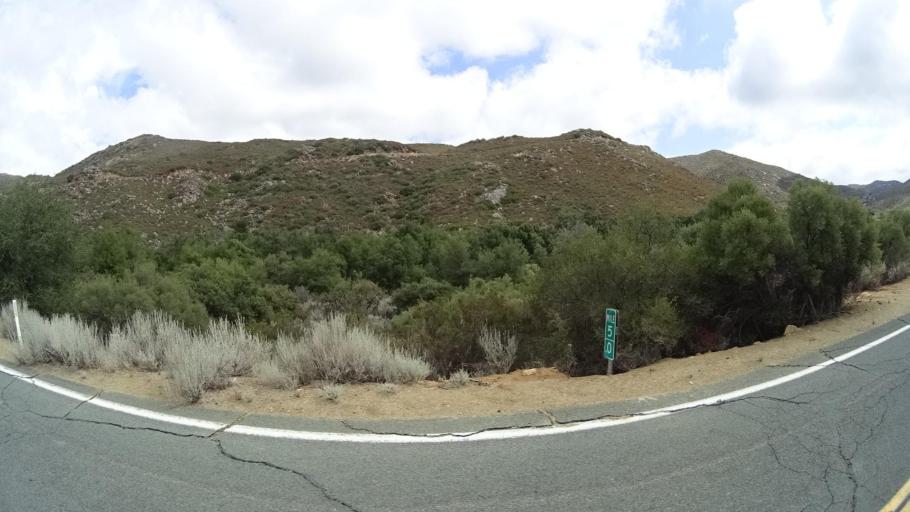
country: US
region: California
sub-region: San Diego County
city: Pine Valley
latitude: 32.7818
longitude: -116.4499
